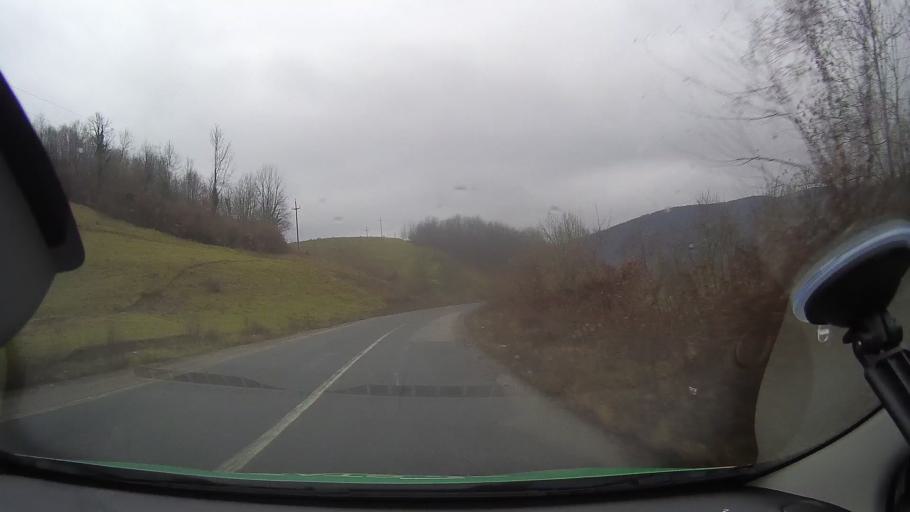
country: RO
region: Arad
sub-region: Comuna Halmagiu
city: Halmagiu
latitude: 46.2420
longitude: 22.5632
